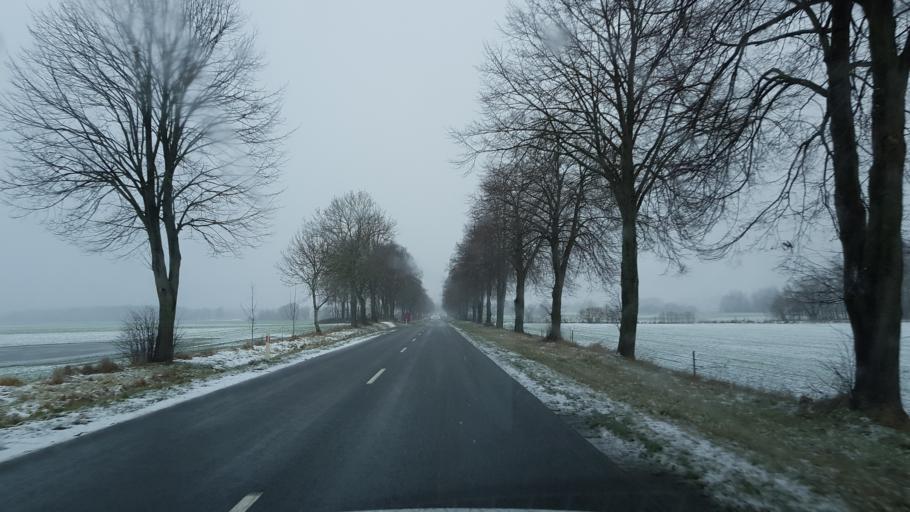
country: PL
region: West Pomeranian Voivodeship
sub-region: Powiat gryficki
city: Gryfice
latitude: 53.9418
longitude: 15.1422
